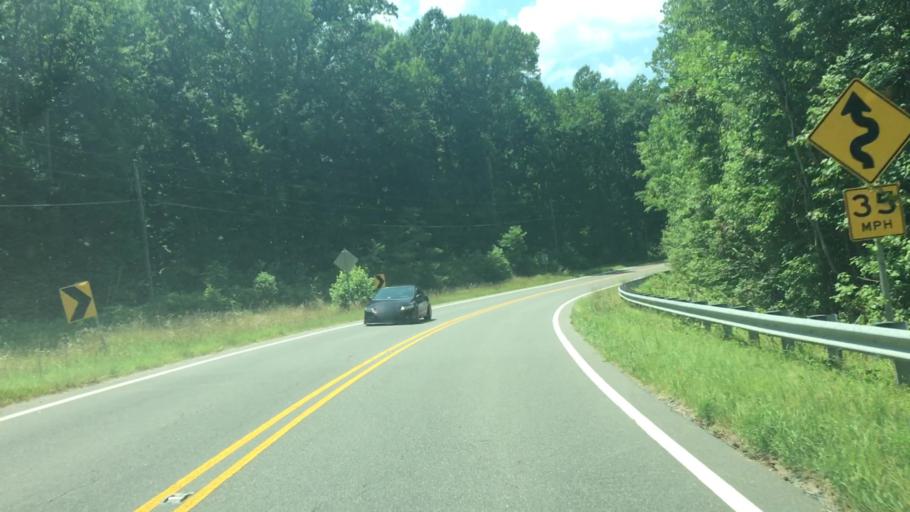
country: US
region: Virginia
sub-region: King George County
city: King George
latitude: 38.3101
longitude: -77.2312
